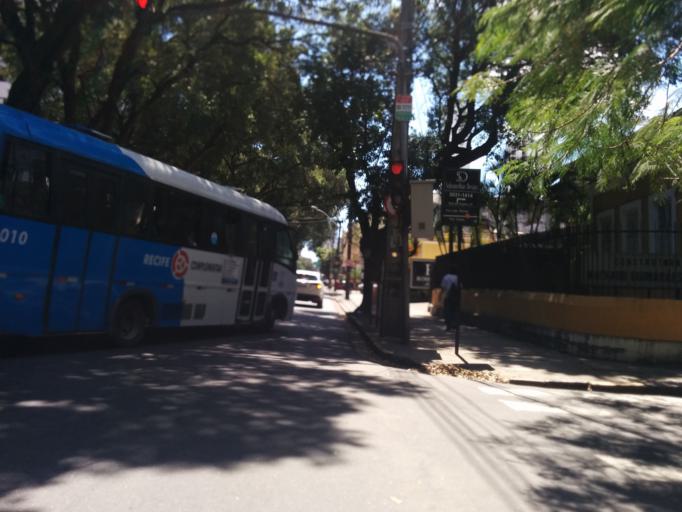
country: BR
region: Pernambuco
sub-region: Recife
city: Recife
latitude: -8.0452
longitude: -34.8984
